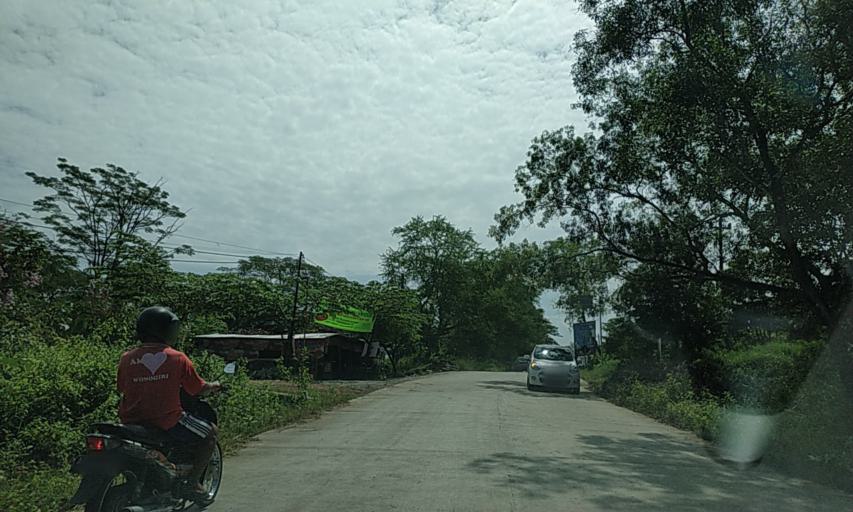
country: ID
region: Central Java
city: Selogiri
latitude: -7.8350
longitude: 110.9227
